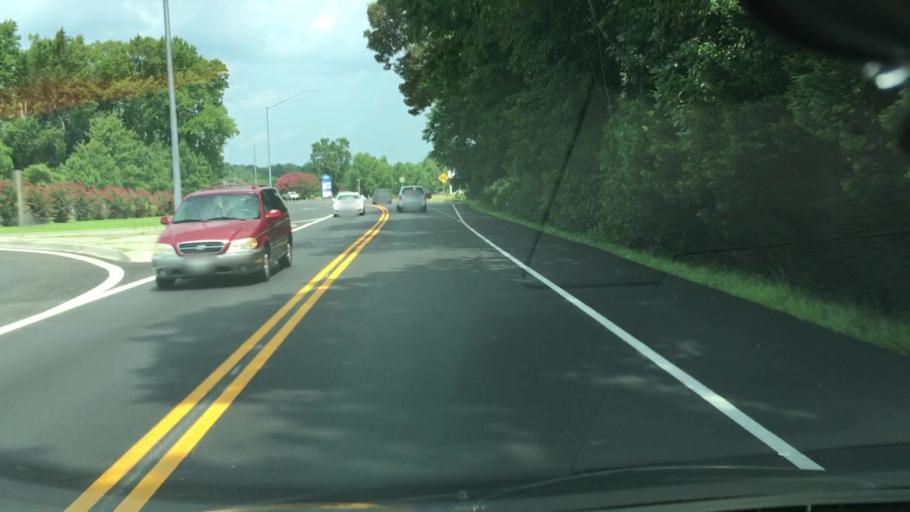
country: US
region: Maryland
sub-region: Worcester County
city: Ocean Pines
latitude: 38.3733
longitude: -75.1633
